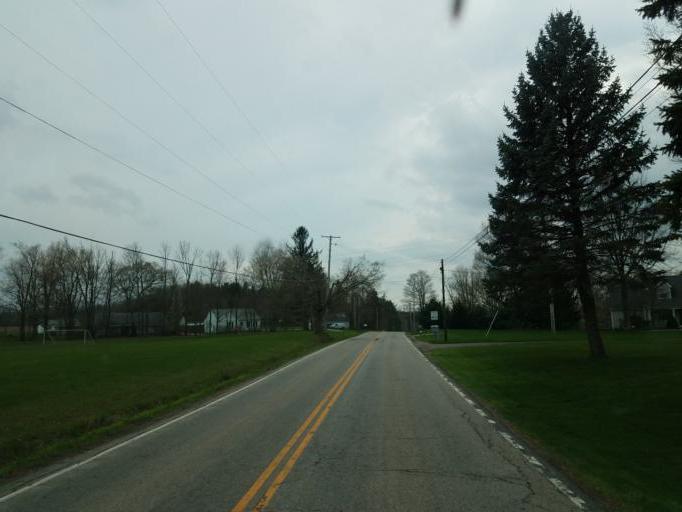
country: US
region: Ohio
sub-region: Richland County
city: Lexington
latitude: 40.7113
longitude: -82.5718
